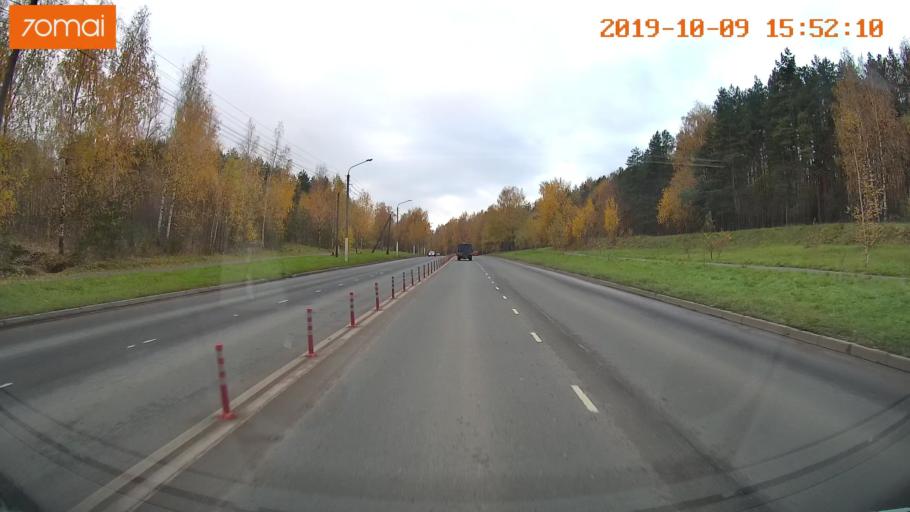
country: RU
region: Kostroma
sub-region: Kostromskoy Rayon
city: Kostroma
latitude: 57.7917
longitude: 40.9714
